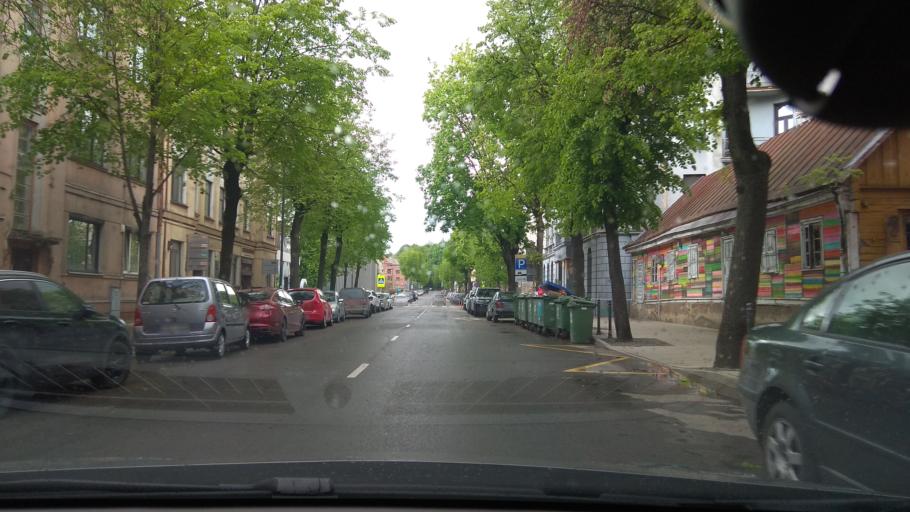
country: LT
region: Kauno apskritis
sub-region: Kaunas
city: Kaunas
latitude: 54.9006
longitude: 23.9157
